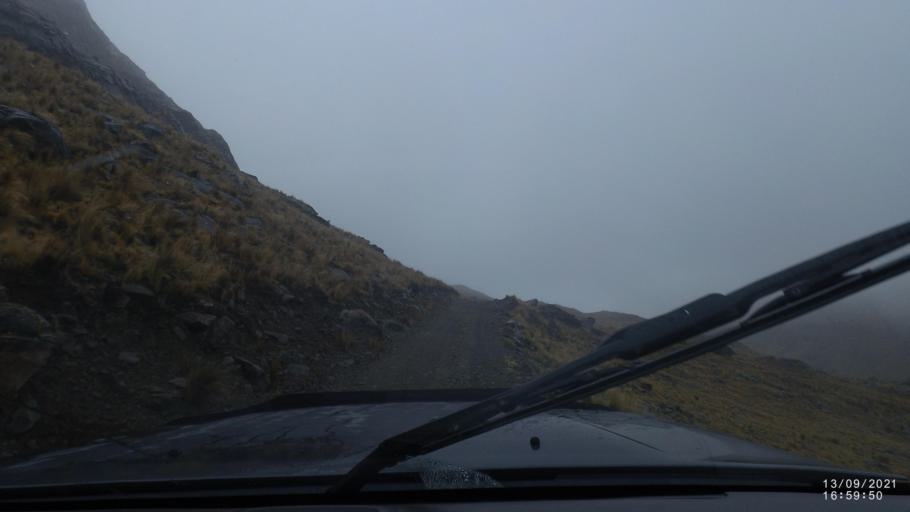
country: BO
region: Cochabamba
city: Colomi
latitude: -17.3115
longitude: -65.7165
